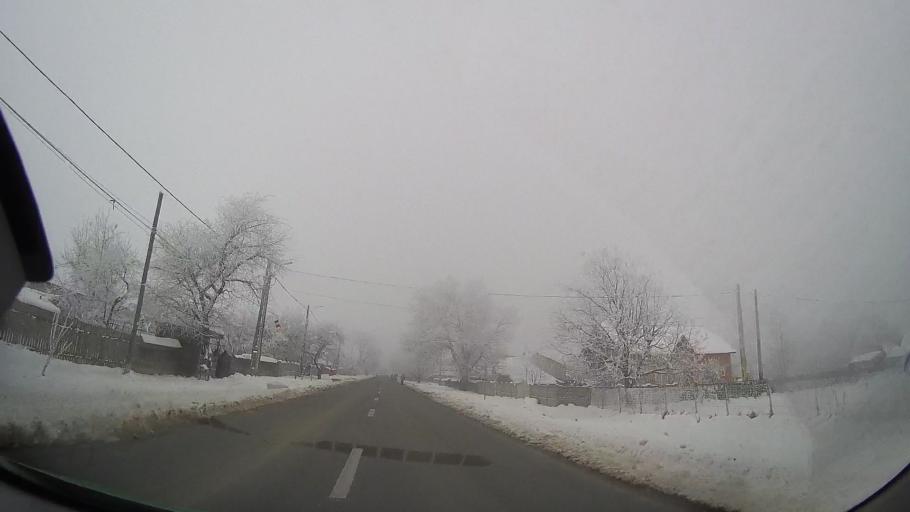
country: RO
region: Iasi
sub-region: Comuna Mogosesti-Siret
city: Mogosesti-Siret
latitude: 47.1597
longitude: 26.7744
